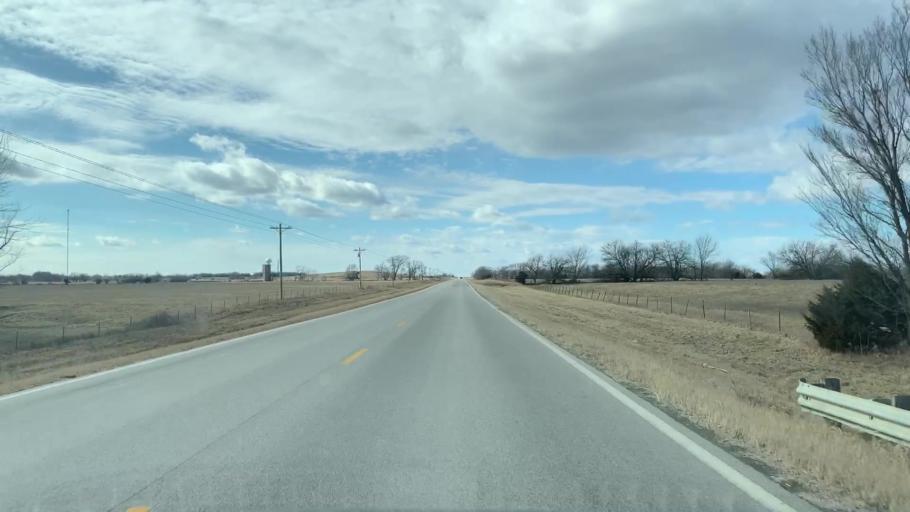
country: US
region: Kansas
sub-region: Neosho County
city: Erie
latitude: 37.5294
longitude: -95.3443
